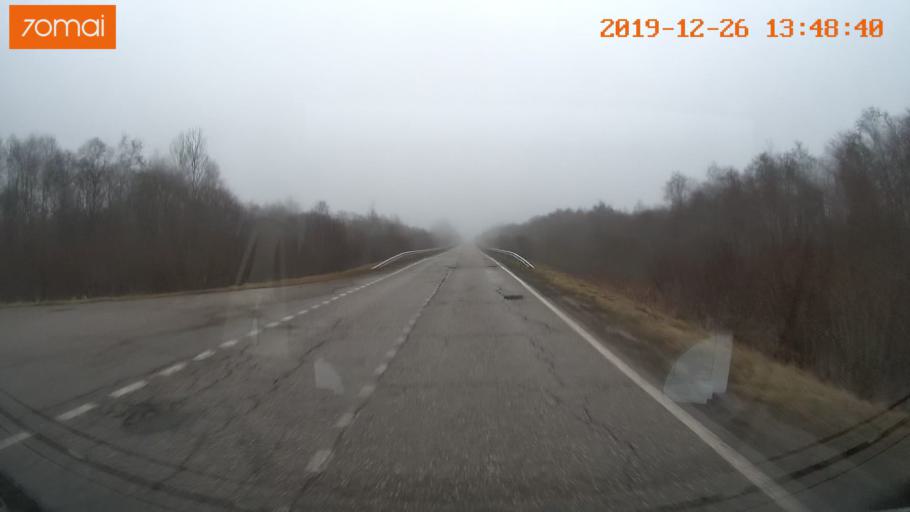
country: RU
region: Vologda
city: Sheksna
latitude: 58.6734
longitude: 38.5521
